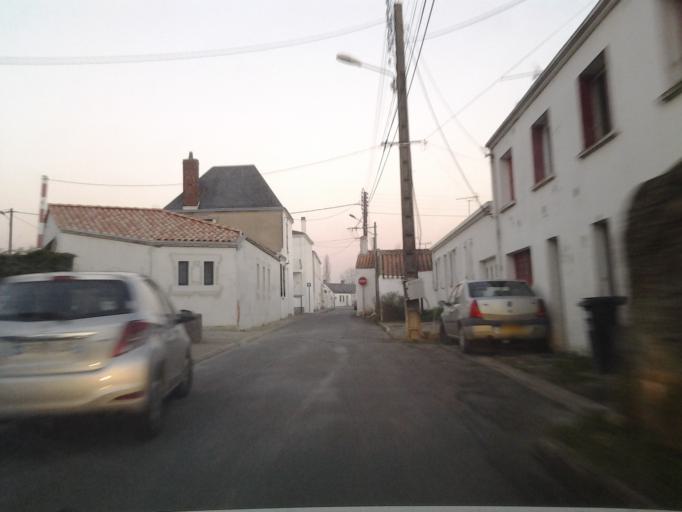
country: FR
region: Pays de la Loire
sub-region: Departement de la Vendee
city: Beauvoir-sur-Mer
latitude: 46.9141
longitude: -2.0450
